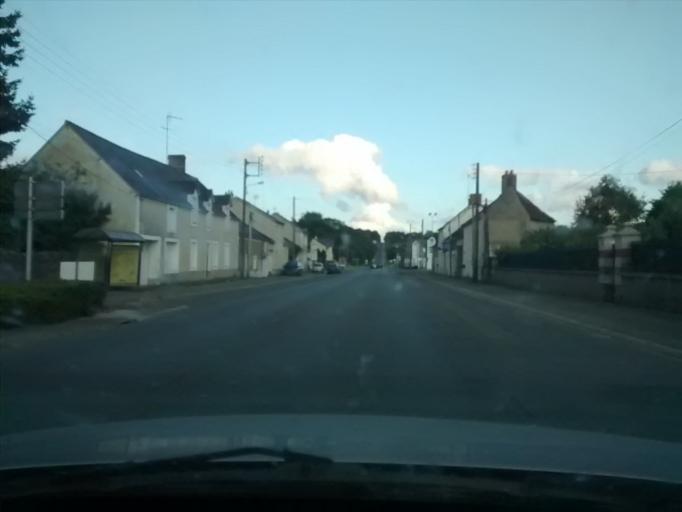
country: FR
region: Pays de la Loire
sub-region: Departement de la Sarthe
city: Sille-le-Guillaume
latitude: 48.1818
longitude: -0.1243
